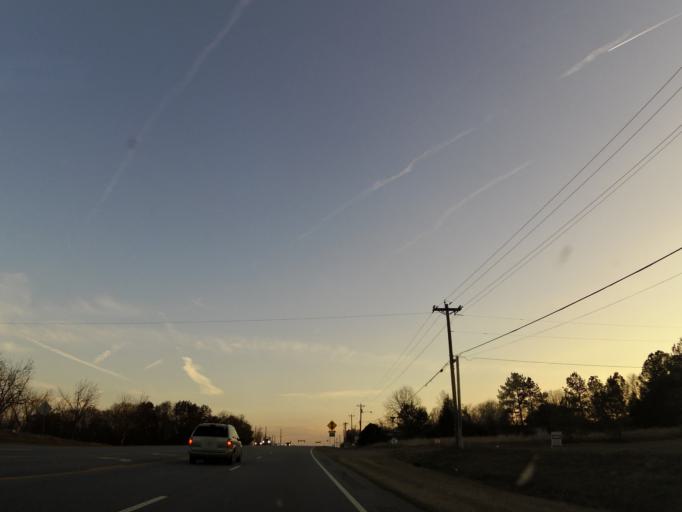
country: US
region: Georgia
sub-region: Lee County
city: Leesburg
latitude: 31.6824
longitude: -84.1728
